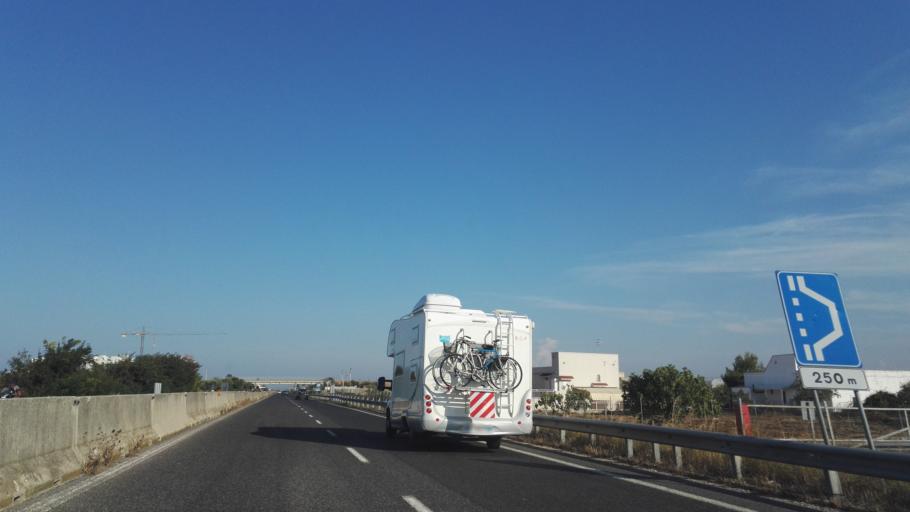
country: IT
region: Apulia
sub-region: Provincia di Bari
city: Monopoli
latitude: 40.9339
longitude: 17.2956
